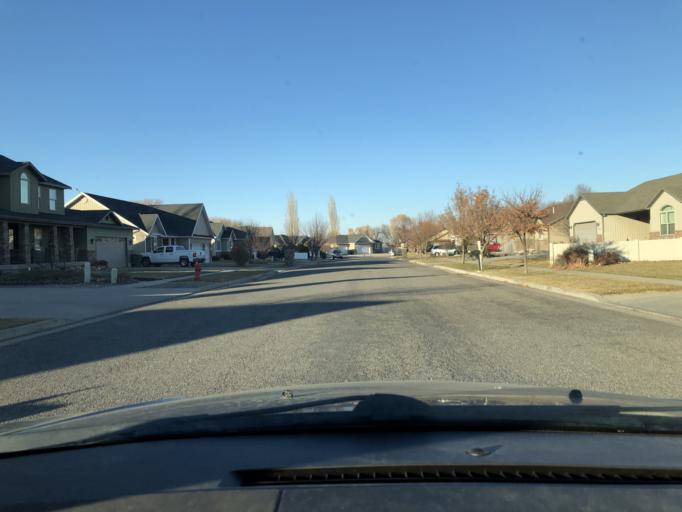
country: US
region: Utah
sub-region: Cache County
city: Wellsville
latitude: 41.6514
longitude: -111.9126
